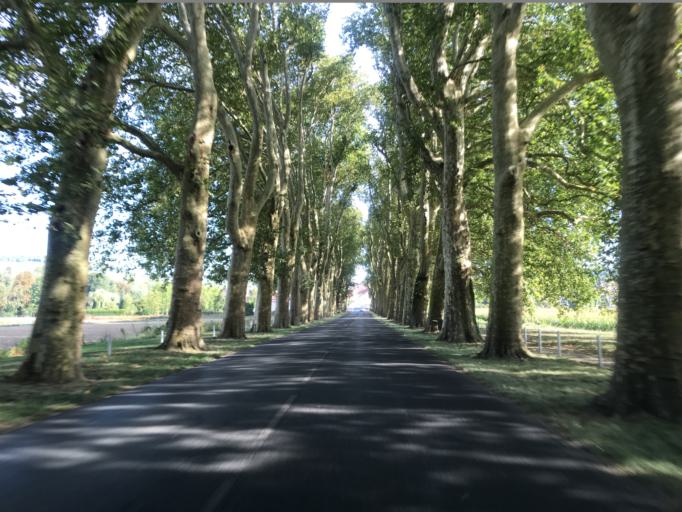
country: FR
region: Champagne-Ardenne
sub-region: Departement de la Marne
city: Damery
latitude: 49.0665
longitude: 3.8759
